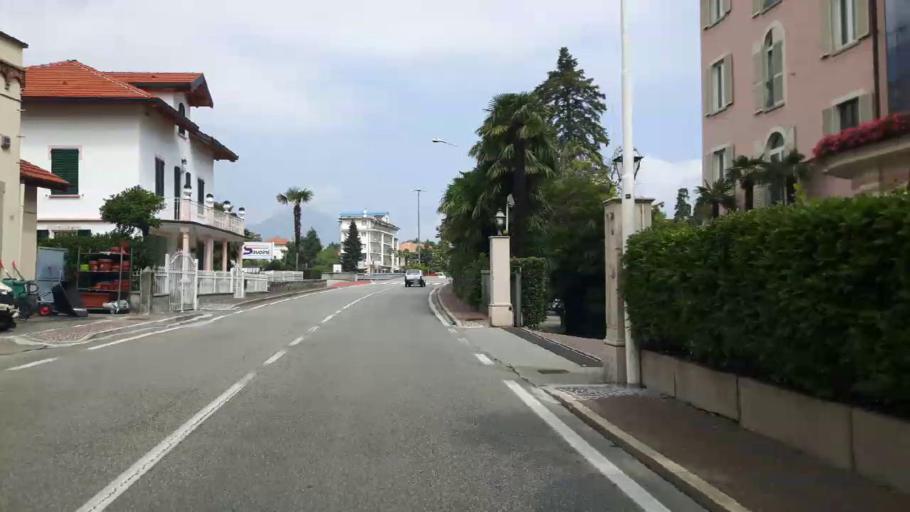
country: IT
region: Piedmont
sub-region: Provincia Verbano-Cusio-Ossola
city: Baveno
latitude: 45.9117
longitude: 8.5032
